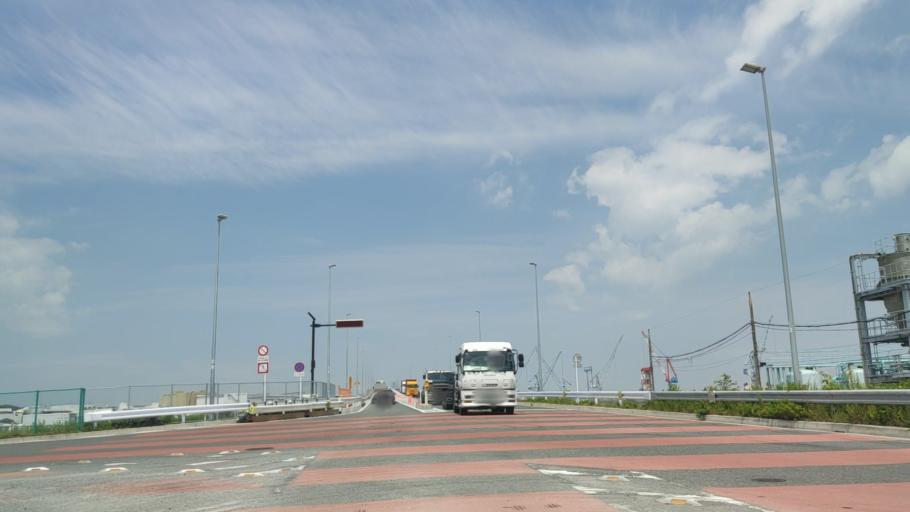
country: JP
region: Kanagawa
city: Yokohama
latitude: 35.4085
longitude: 139.6853
